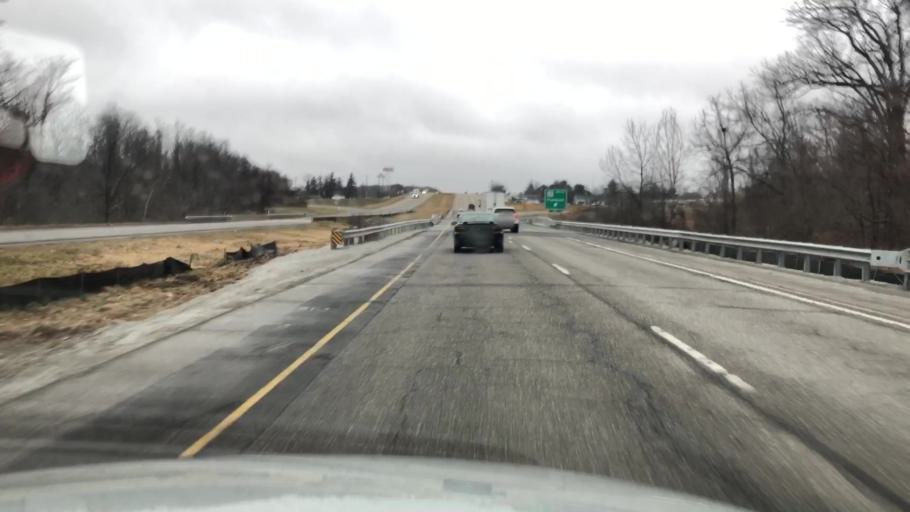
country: US
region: Indiana
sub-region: Marshall County
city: Plymouth
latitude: 41.3625
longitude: -86.3056
